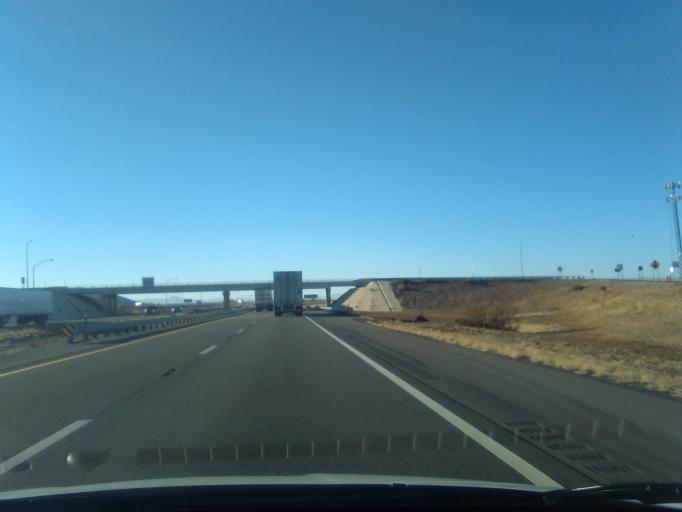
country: US
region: New Mexico
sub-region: Hidalgo County
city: Lordsburg
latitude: 32.3522
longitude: -108.7389
